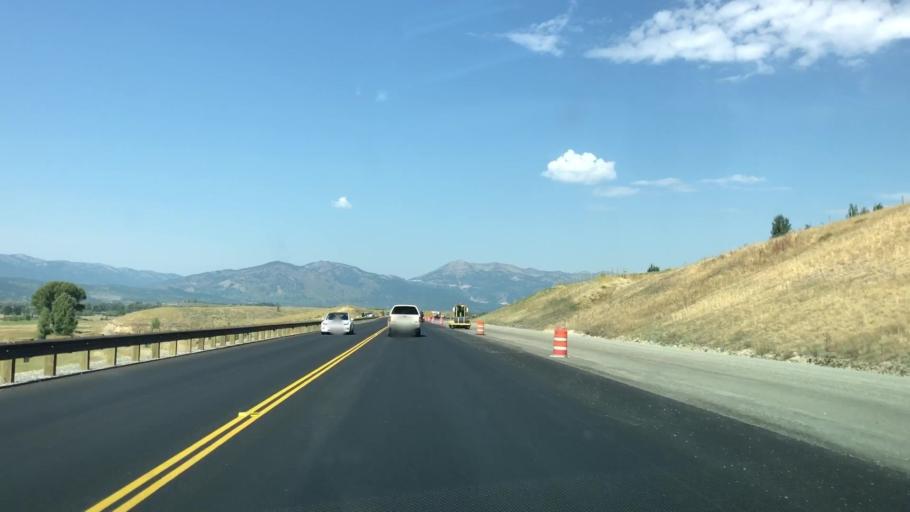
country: US
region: Wyoming
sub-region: Teton County
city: South Park
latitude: 43.4090
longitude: -110.7651
